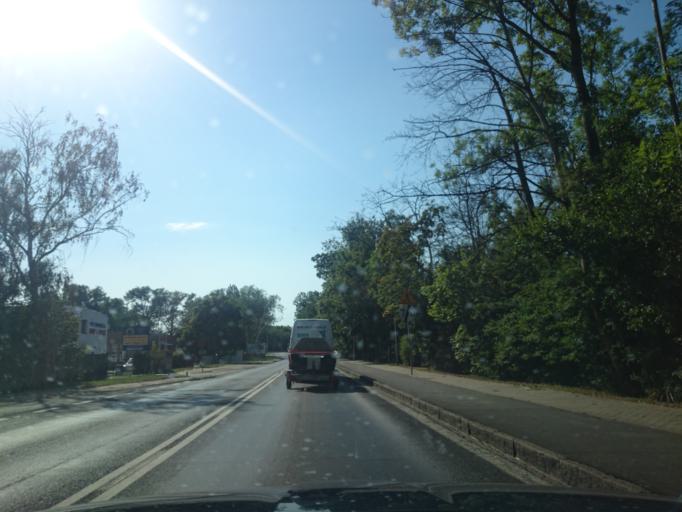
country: PL
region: West Pomeranian Voivodeship
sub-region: Szczecin
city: Szczecin
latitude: 53.3971
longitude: 14.6204
